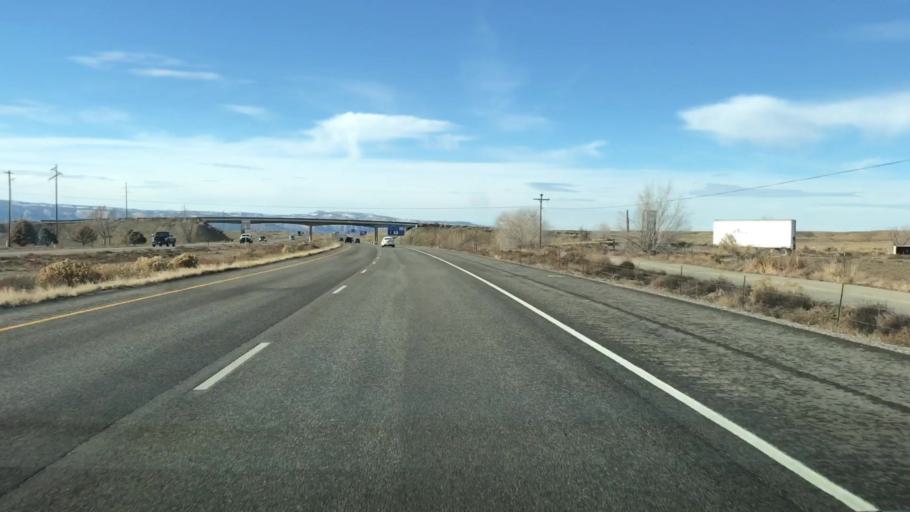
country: US
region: Colorado
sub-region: Mesa County
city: Fruitvale
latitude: 39.1087
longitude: -108.5084
